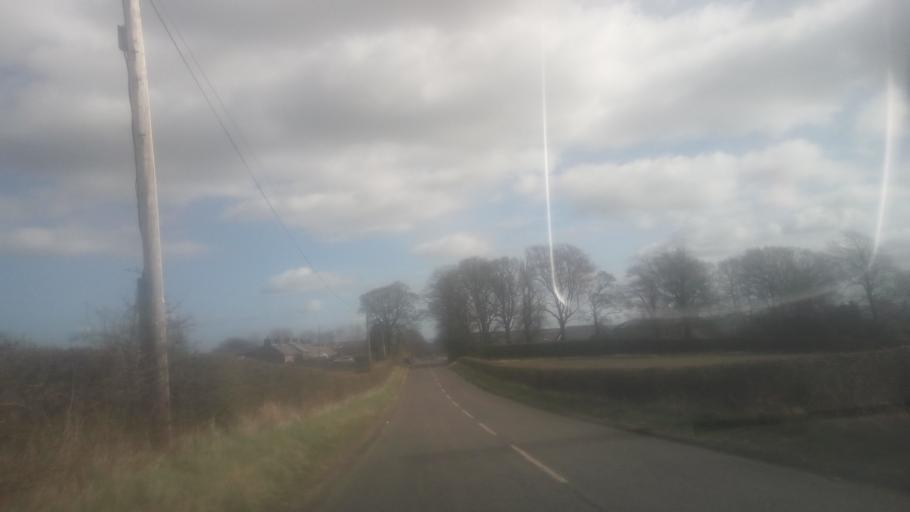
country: GB
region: Scotland
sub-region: East Lothian
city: Tranent
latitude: 55.9271
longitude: -2.9663
